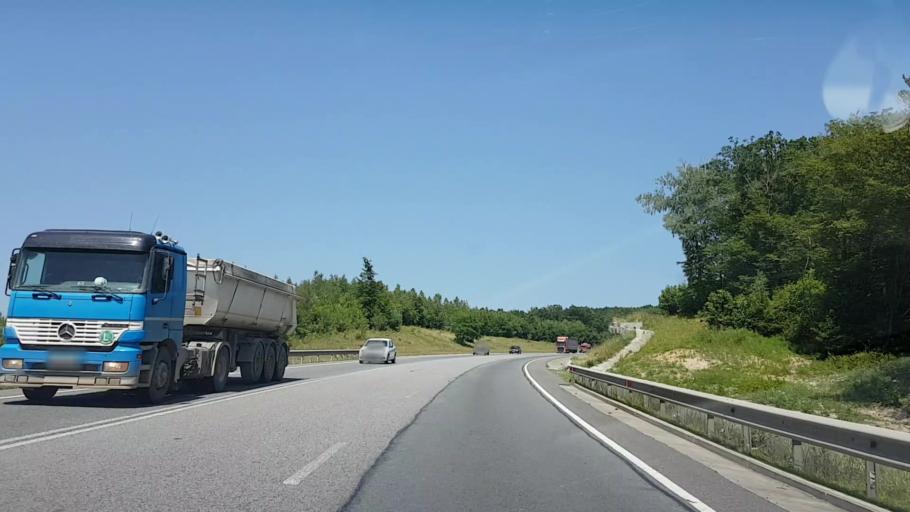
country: RO
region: Cluj
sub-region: Comuna Feleacu
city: Feleacu
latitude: 46.7071
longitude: 23.6433
